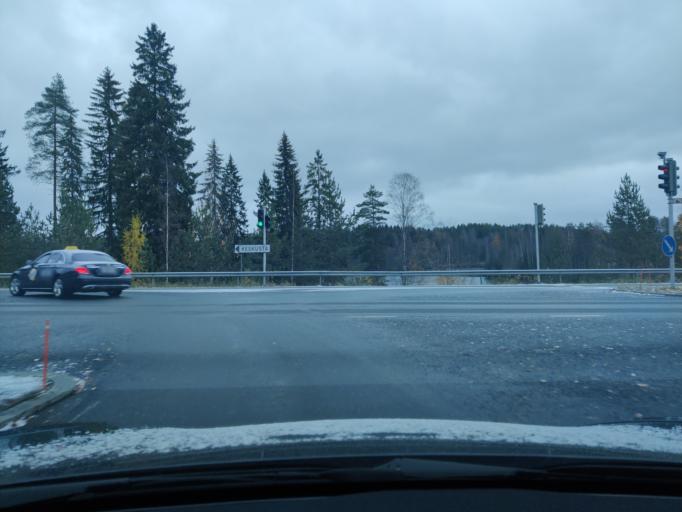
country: FI
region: Northern Savo
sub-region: Kuopio
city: Kuopio
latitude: 62.8422
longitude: 27.6339
